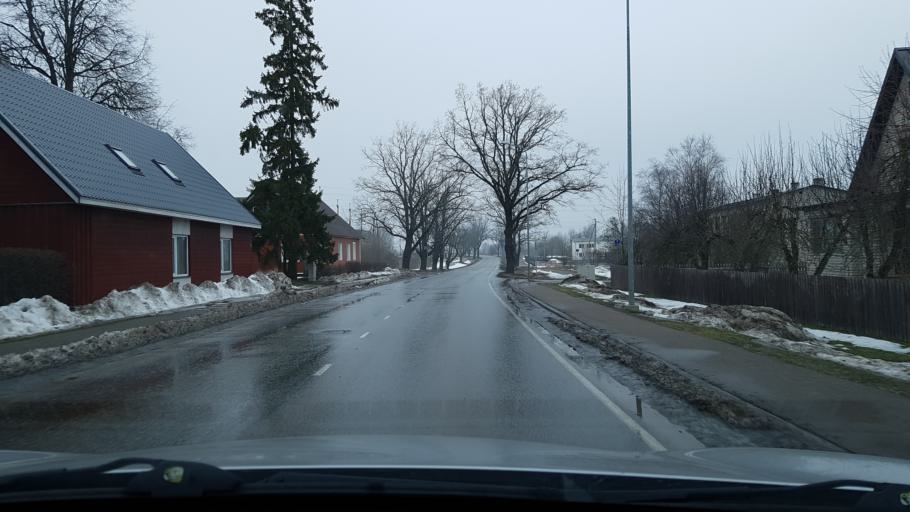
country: EE
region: Valgamaa
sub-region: Torva linn
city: Torva
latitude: 58.2398
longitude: 25.8578
